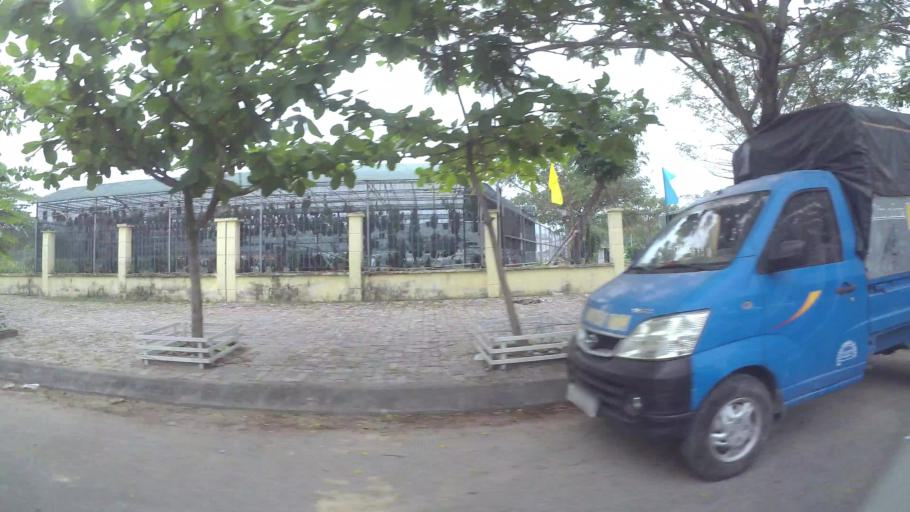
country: VN
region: Da Nang
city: Thanh Khe
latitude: 16.0601
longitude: 108.1836
